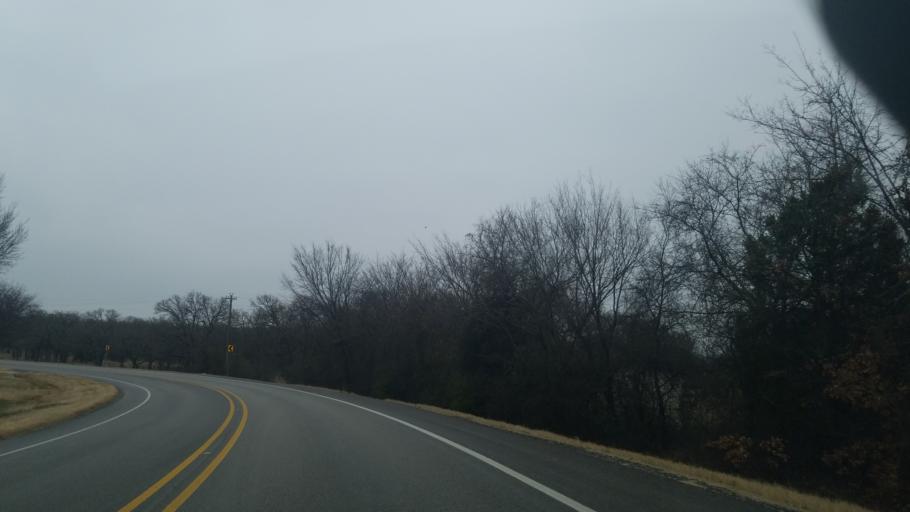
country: US
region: Texas
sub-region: Denton County
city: Argyle
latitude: 33.1335
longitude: -97.1486
